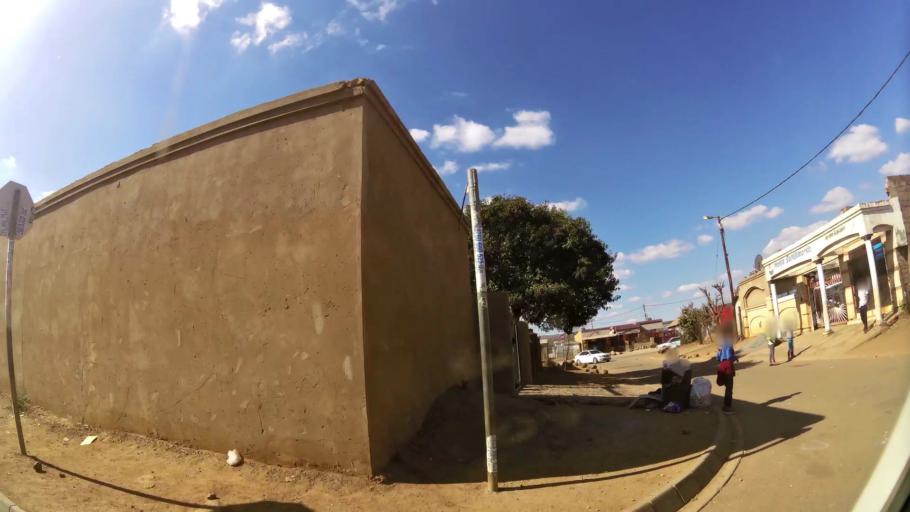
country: ZA
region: Gauteng
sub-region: City of Tshwane Metropolitan Municipality
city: Cullinan
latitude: -25.7195
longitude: 28.4072
